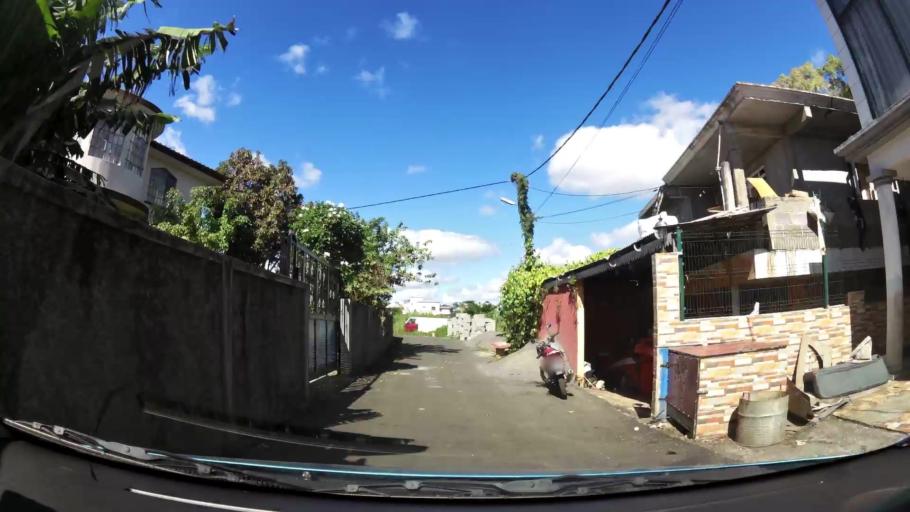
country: MU
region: Plaines Wilhems
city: Vacoas
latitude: -20.2937
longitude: 57.4775
